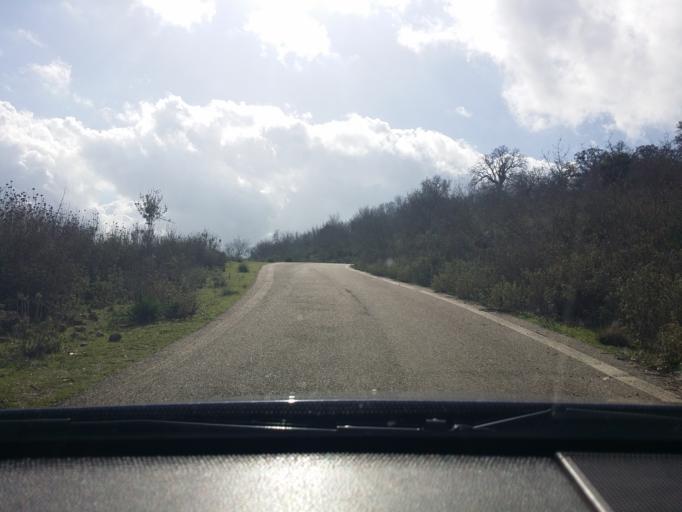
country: GR
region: West Greece
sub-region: Nomos Aitolias kai Akarnanias
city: Fitiai
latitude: 38.6404
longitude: 21.1959
